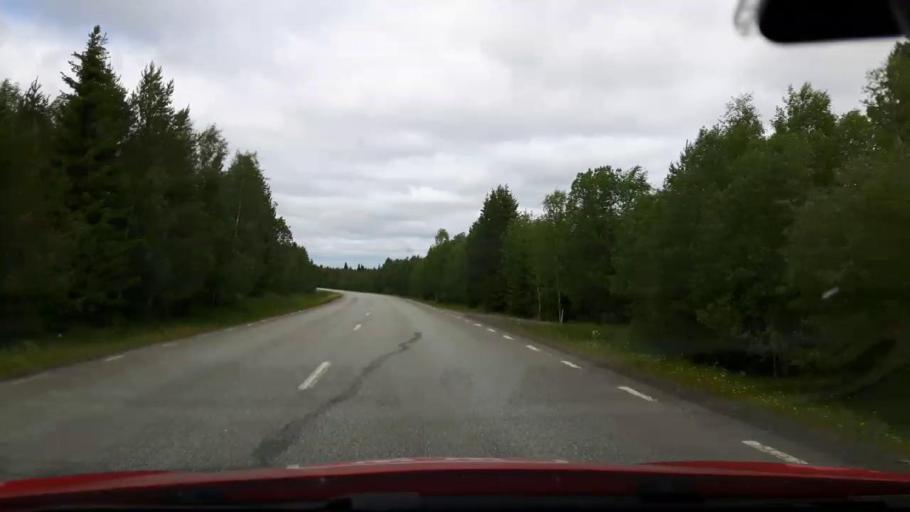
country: SE
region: Jaemtland
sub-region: Krokoms Kommun
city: Krokom
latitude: 63.3818
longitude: 14.5074
